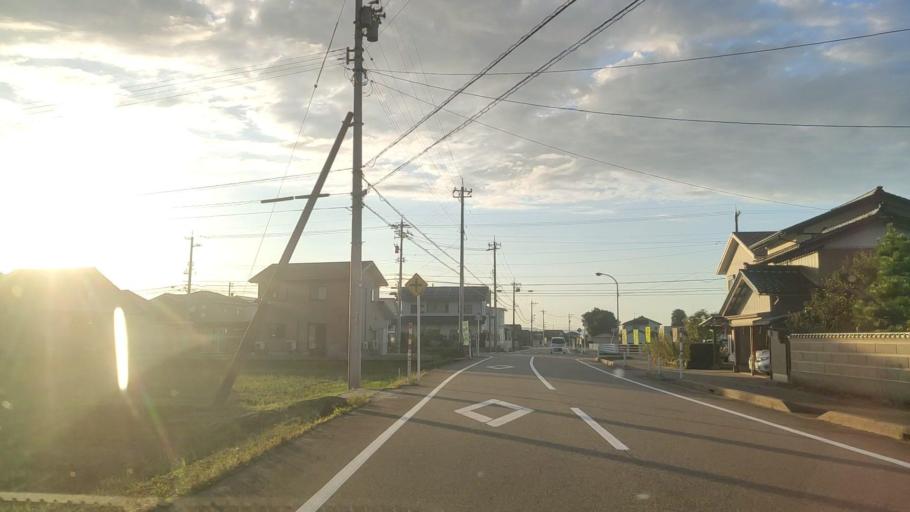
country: JP
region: Toyama
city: Nanto-shi
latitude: 36.5965
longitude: 136.9473
